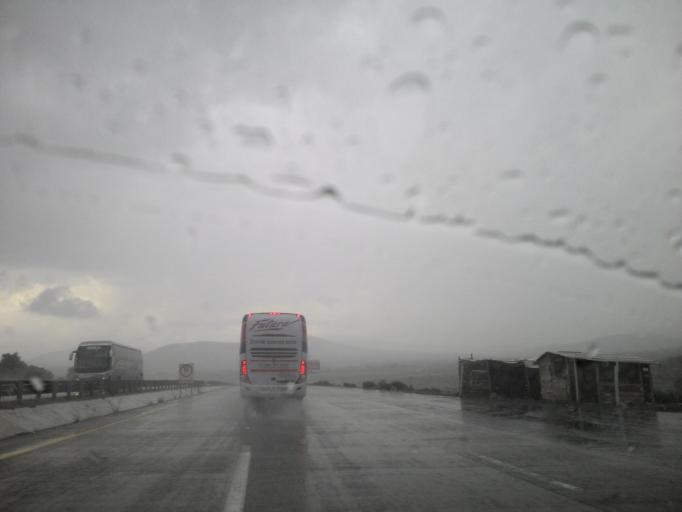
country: MX
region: Hidalgo
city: Zempoala
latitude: 19.8863
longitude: -98.6409
